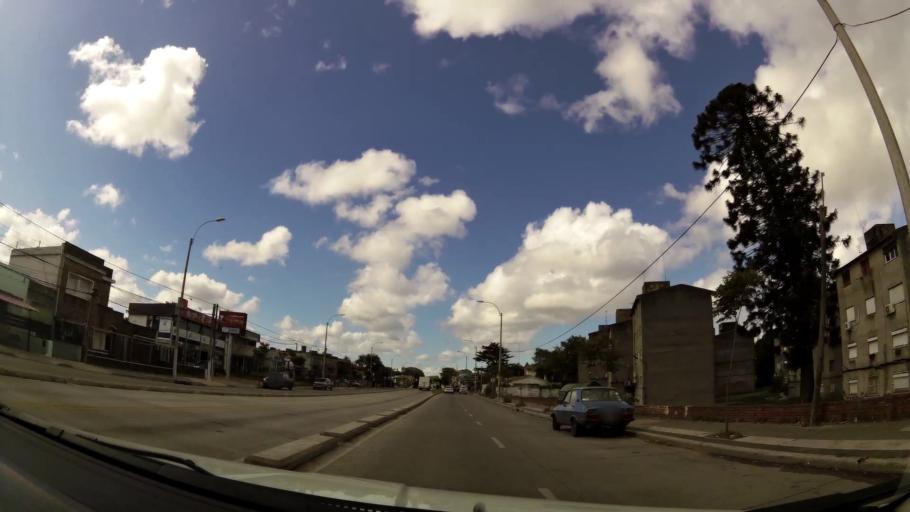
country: UY
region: Montevideo
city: Montevideo
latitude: -34.8503
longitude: -56.2237
